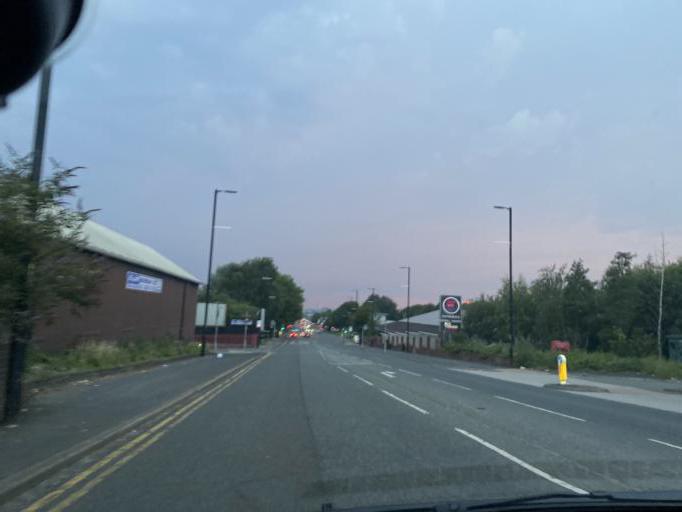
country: GB
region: England
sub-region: Borough of Tameside
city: Droylsden
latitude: 53.4730
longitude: -2.1730
